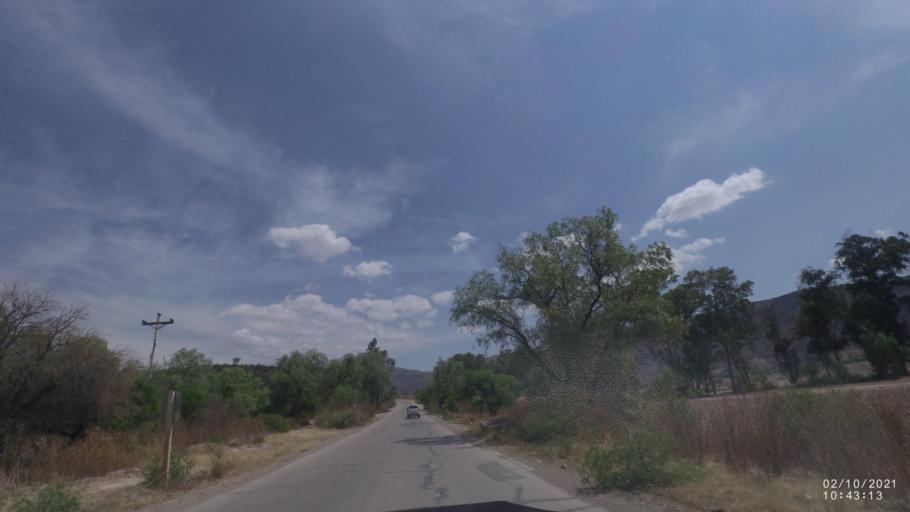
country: BO
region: Cochabamba
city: Capinota
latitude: -17.5992
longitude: -66.2977
